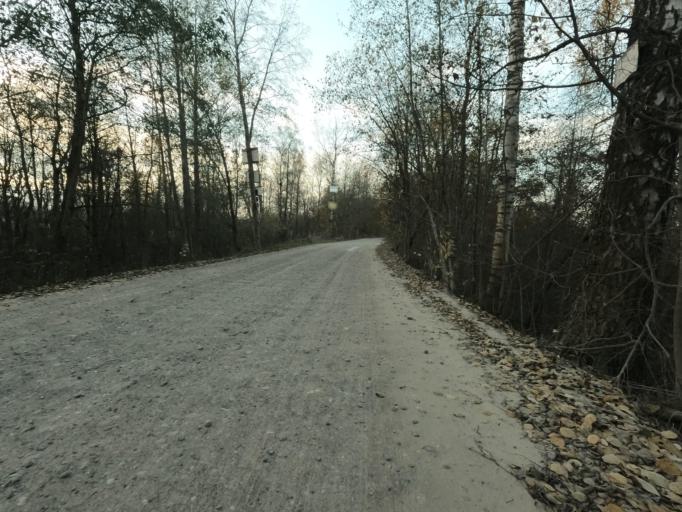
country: RU
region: Leningrad
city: Mga
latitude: 59.7705
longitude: 31.2289
